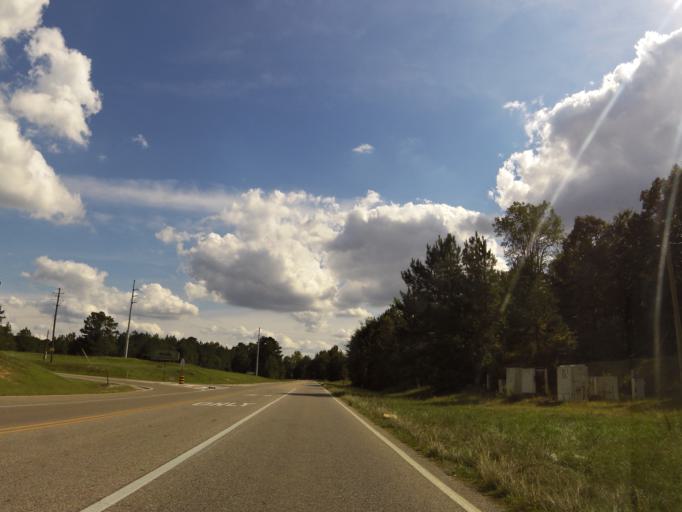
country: US
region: Alabama
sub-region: Dallas County
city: Selmont-West Selmont
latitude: 32.3380
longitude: -86.9966
